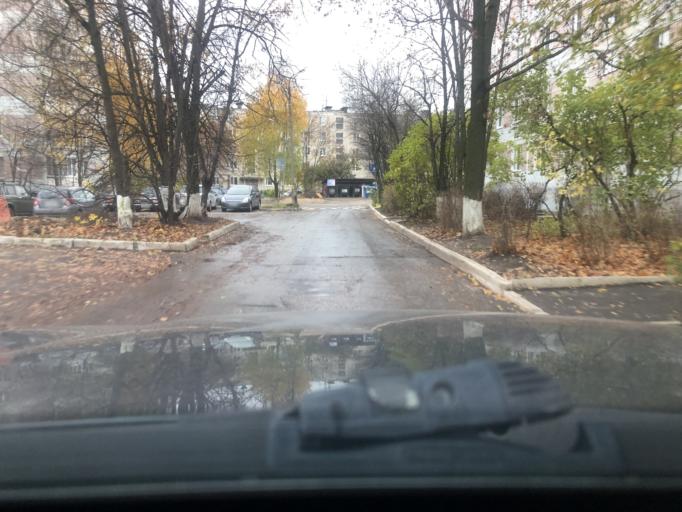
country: RU
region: Moskovskaya
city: Sergiyev Posad
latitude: 56.3226
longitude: 38.1336
